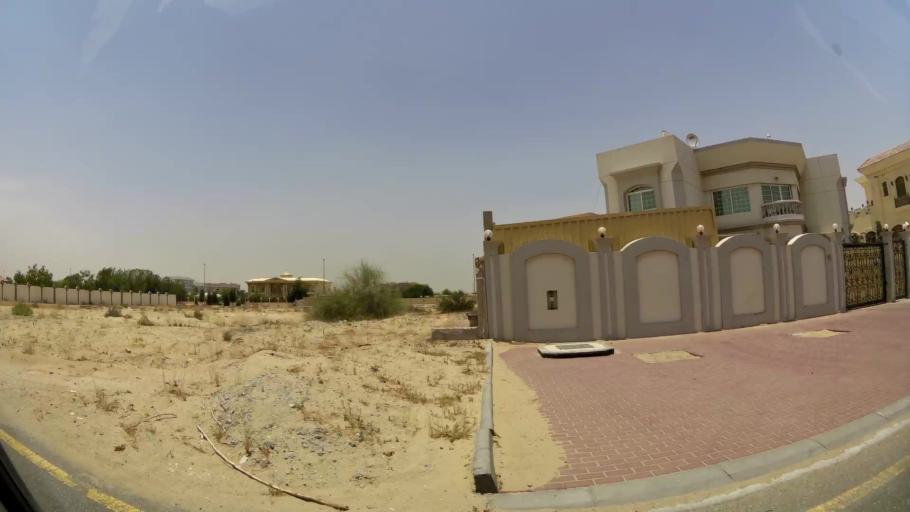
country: AE
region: Ash Shariqah
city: Sharjah
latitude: 25.2345
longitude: 55.4529
